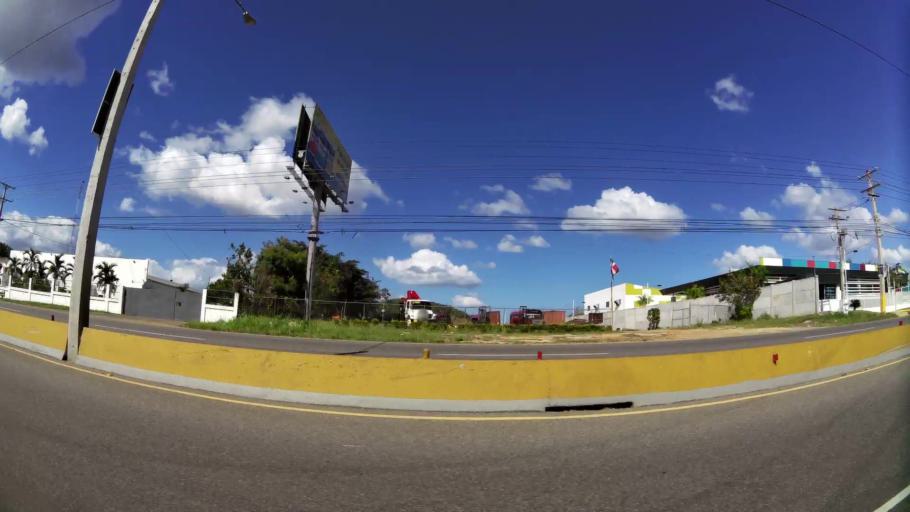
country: DO
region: Santo Domingo
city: Santo Domingo Oeste
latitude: 18.5598
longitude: -70.0600
